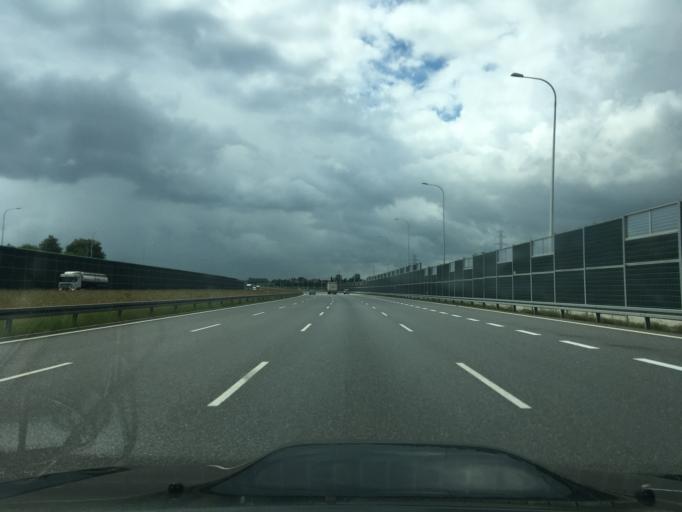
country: PL
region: Lublin Voivodeship
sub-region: Powiat lubelski
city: Lublin
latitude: 51.3029
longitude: 22.5800
